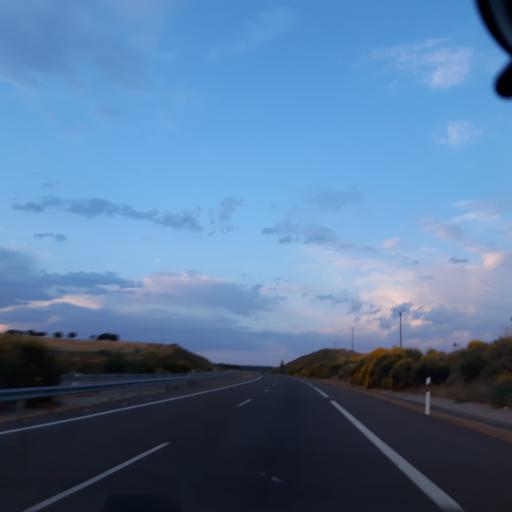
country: ES
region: Castille and Leon
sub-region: Provincia de Salamanca
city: Mozarbez
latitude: 40.8460
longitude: -5.6408
